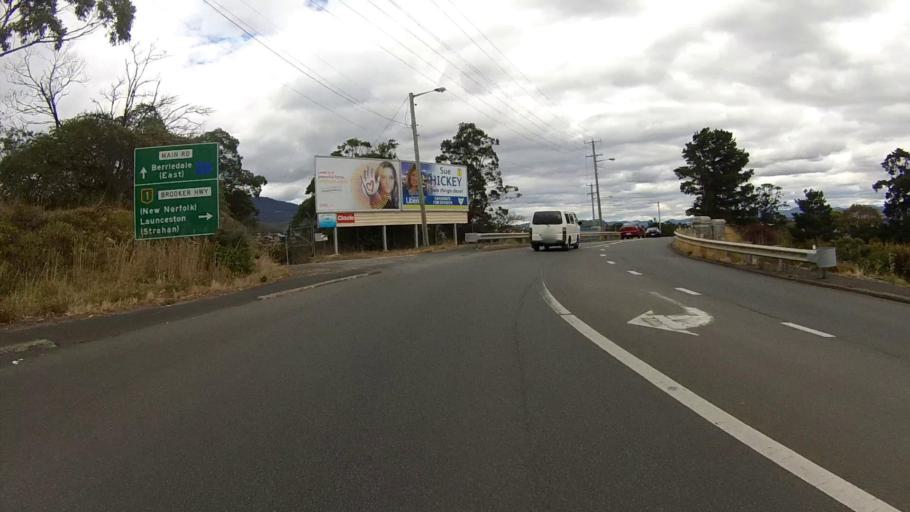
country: AU
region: Tasmania
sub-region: Glenorchy
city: Berriedale
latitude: -42.8201
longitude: 147.2612
